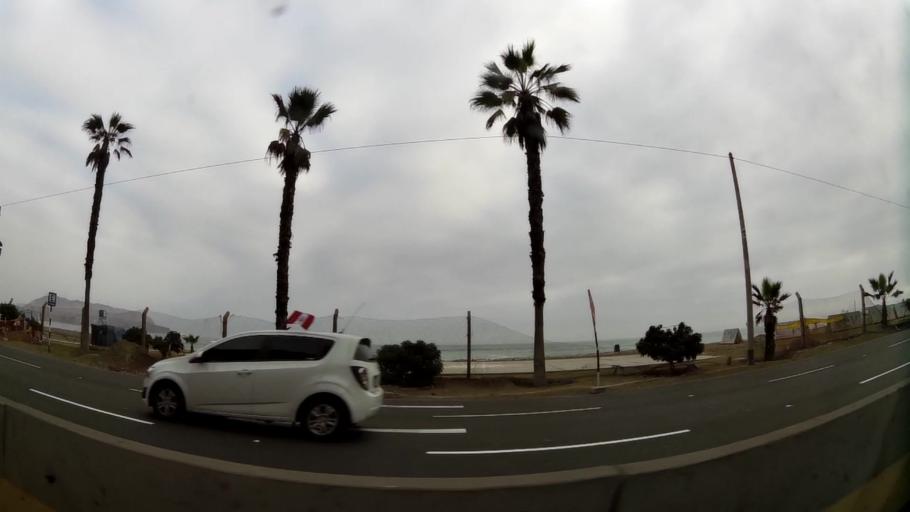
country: PE
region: Lima
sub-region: Lima
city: San Isidro
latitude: -12.1328
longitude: -77.0308
